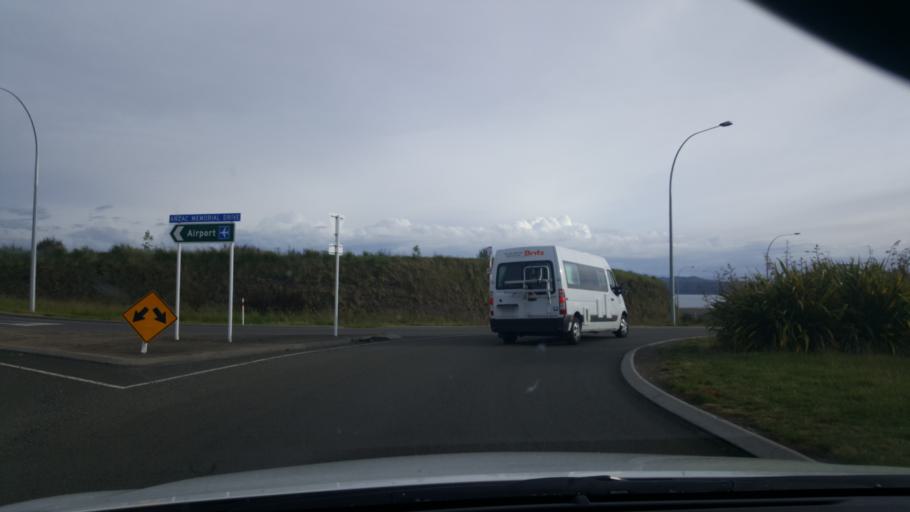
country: NZ
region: Waikato
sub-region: Taupo District
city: Taupo
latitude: -38.7387
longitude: 176.0731
